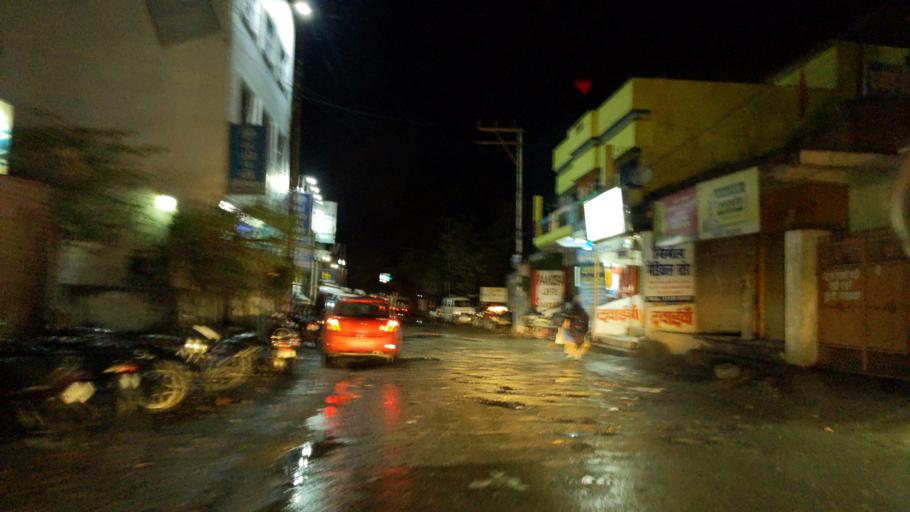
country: IN
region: Uttarakhand
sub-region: Naini Tal
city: Haldwani
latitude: 29.2061
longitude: 79.5171
